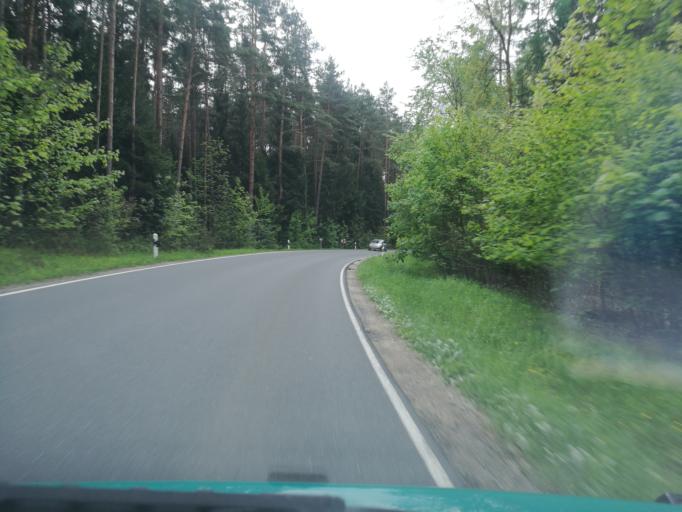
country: DE
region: Bavaria
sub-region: Upper Franconia
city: Sonnefeld
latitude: 50.1994
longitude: 11.1094
